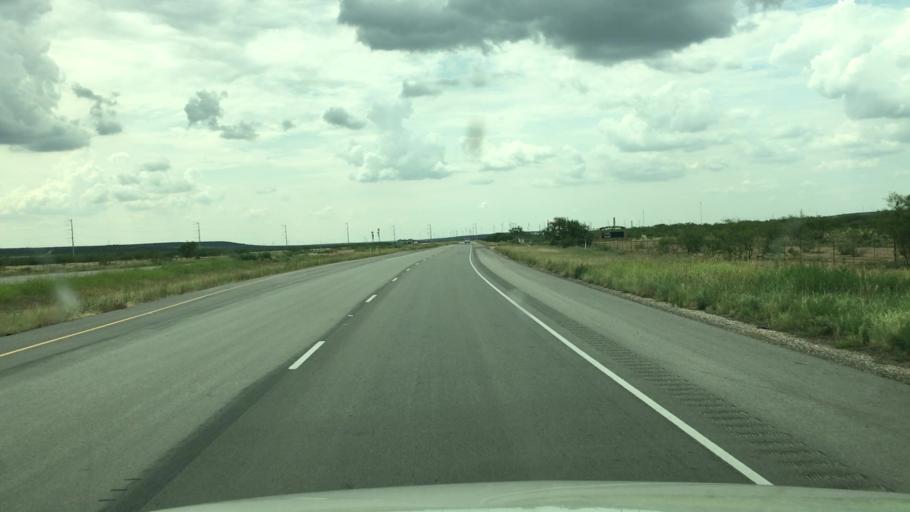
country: US
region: Texas
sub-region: Sterling County
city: Sterling City
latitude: 31.9633
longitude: -101.2213
